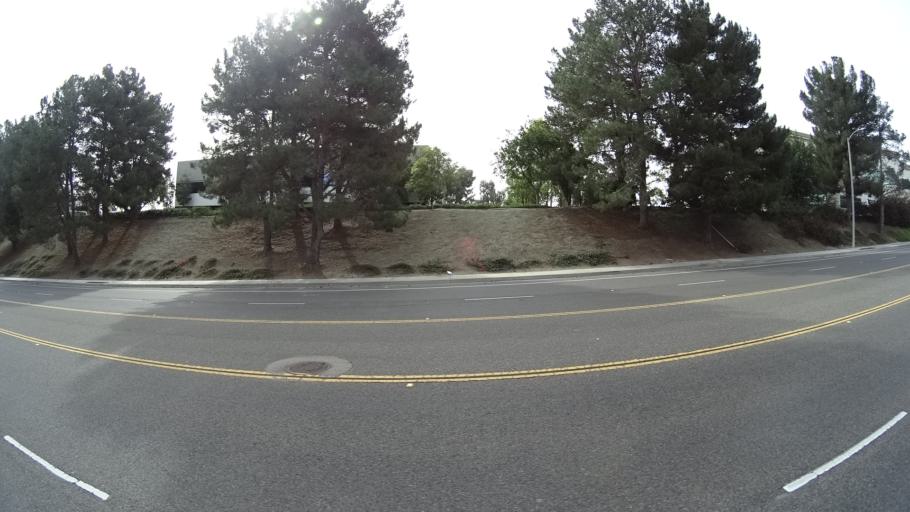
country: US
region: California
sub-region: Orange County
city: Laguna Woods
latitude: 33.5898
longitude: -117.7236
